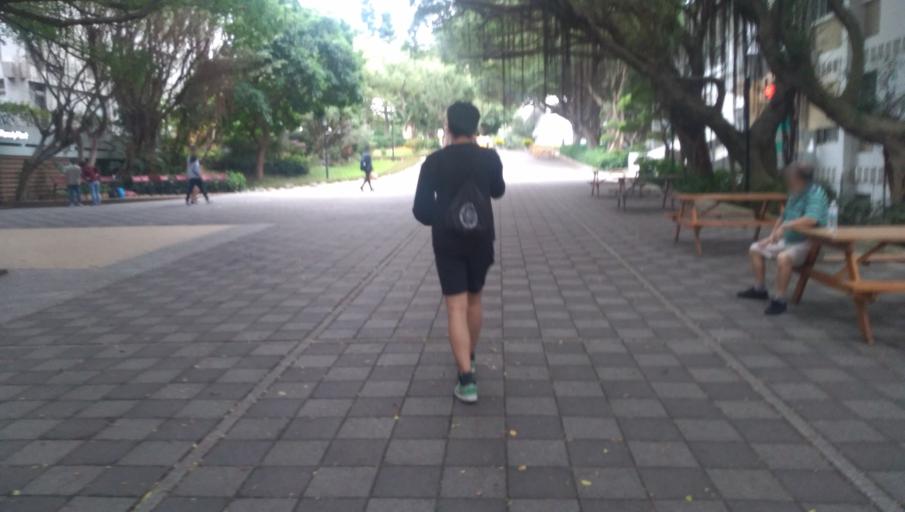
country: TW
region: Taipei
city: Taipei
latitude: 25.1760
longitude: 121.4491
